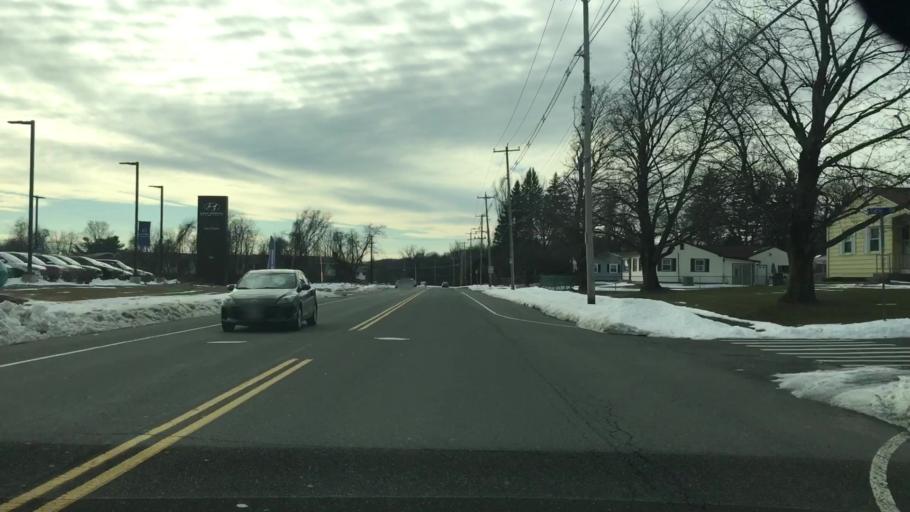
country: US
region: Massachusetts
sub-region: Hampden County
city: Holyoke
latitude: 42.1825
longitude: -72.6379
